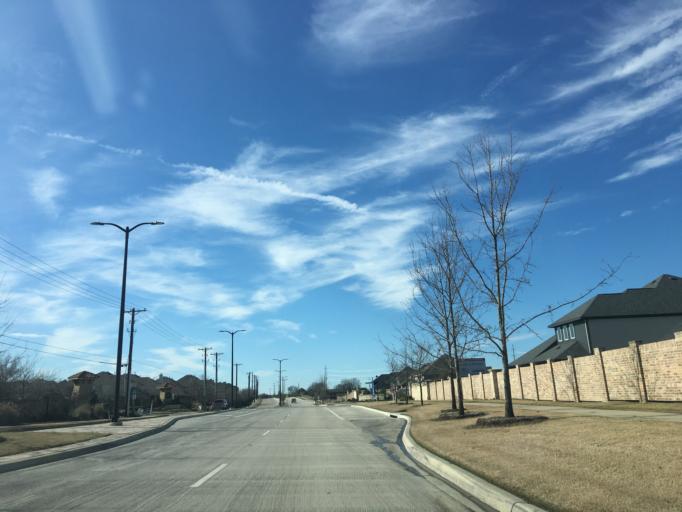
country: US
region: Texas
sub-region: Denton County
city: Little Elm
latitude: 33.2115
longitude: -96.8899
